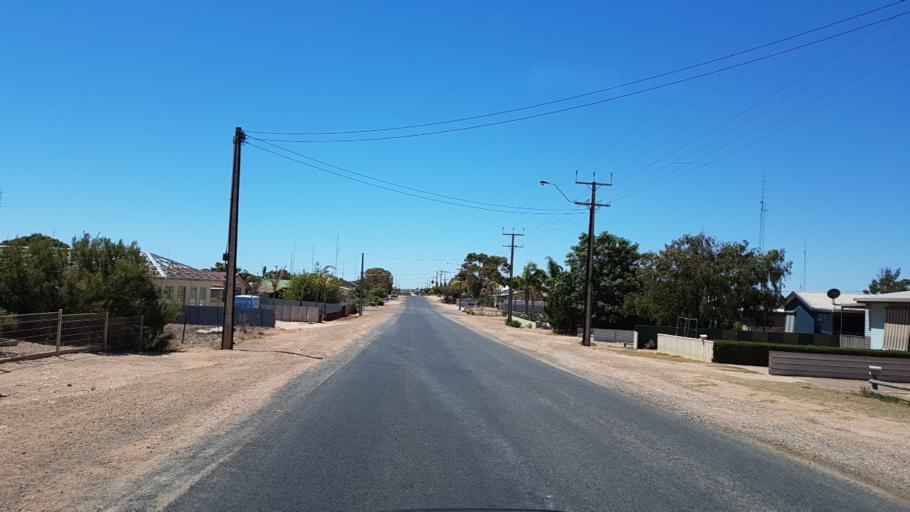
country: AU
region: South Australia
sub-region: Copper Coast
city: Wallaroo
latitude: -34.0518
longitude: 137.5670
